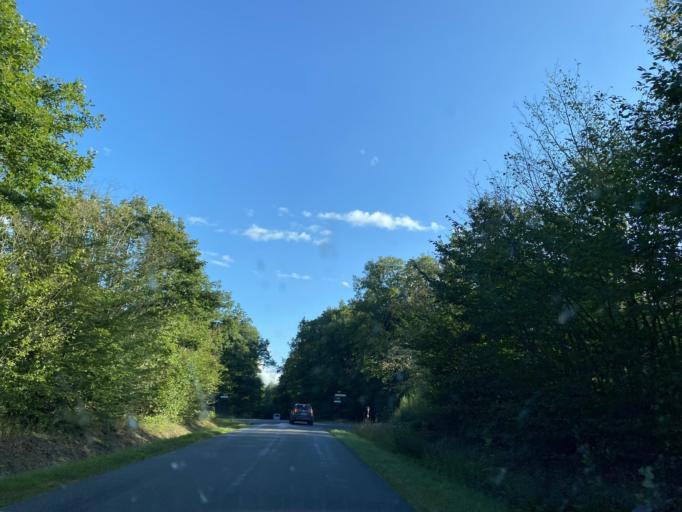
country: FR
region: Auvergne
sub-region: Departement du Puy-de-Dome
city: Randan
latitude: 46.0425
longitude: 3.3236
